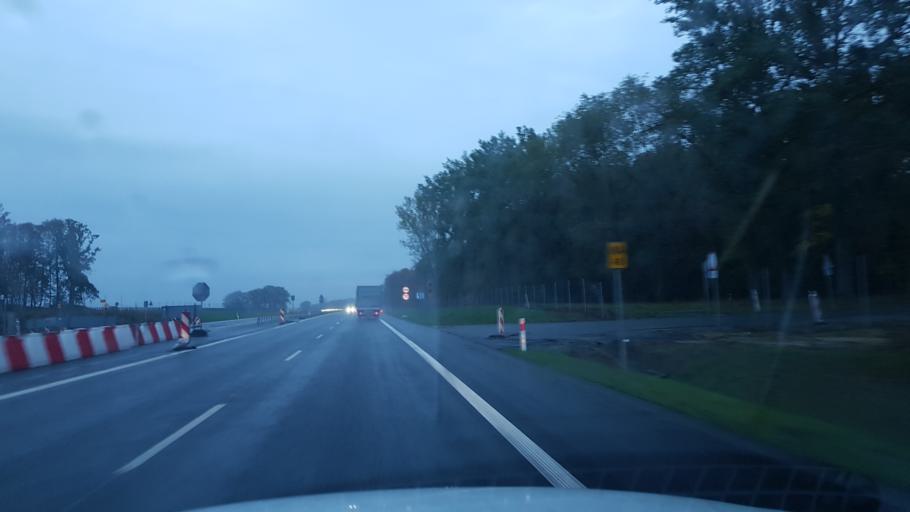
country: PL
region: West Pomeranian Voivodeship
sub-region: Powiat gryficki
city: Ploty
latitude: 53.8360
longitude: 15.3006
